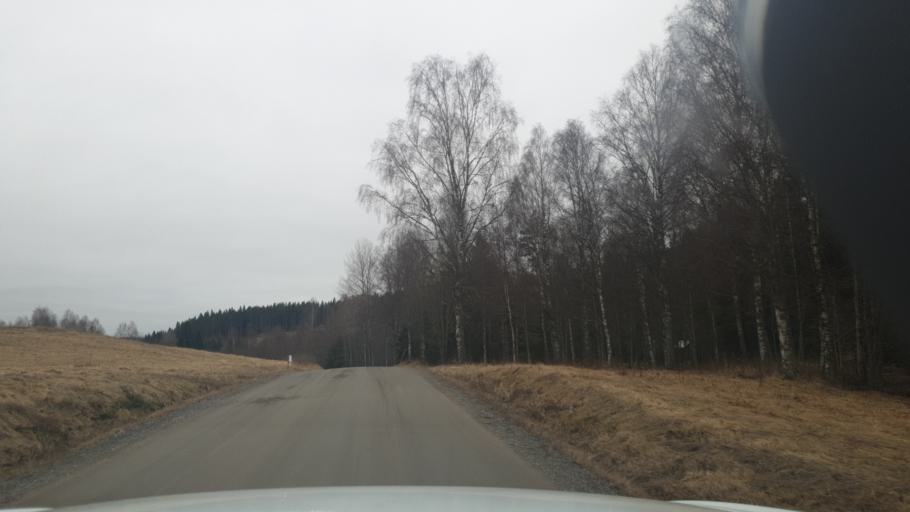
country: NO
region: Ostfold
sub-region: Romskog
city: Romskog
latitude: 59.6853
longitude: 11.9330
